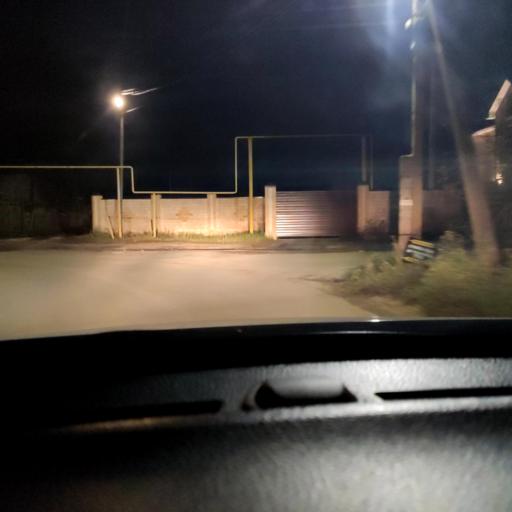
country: RU
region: Voronezj
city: Novaya Usman'
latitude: 51.6811
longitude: 39.3649
